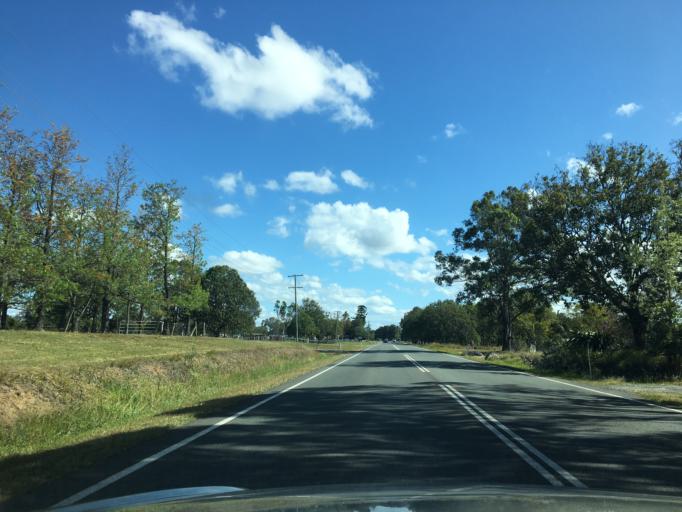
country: AU
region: Queensland
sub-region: Logan
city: Waterford West
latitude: -27.7102
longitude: 153.1314
